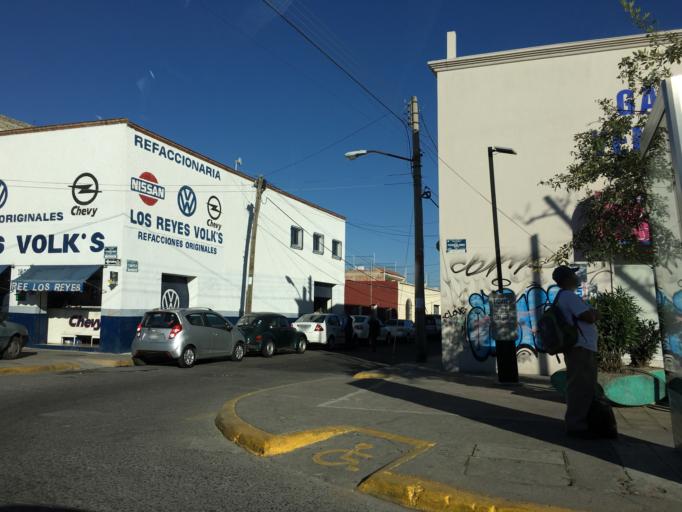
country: MX
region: Jalisco
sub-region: Zapopan
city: Zapopan
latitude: 20.7015
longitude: -103.3548
